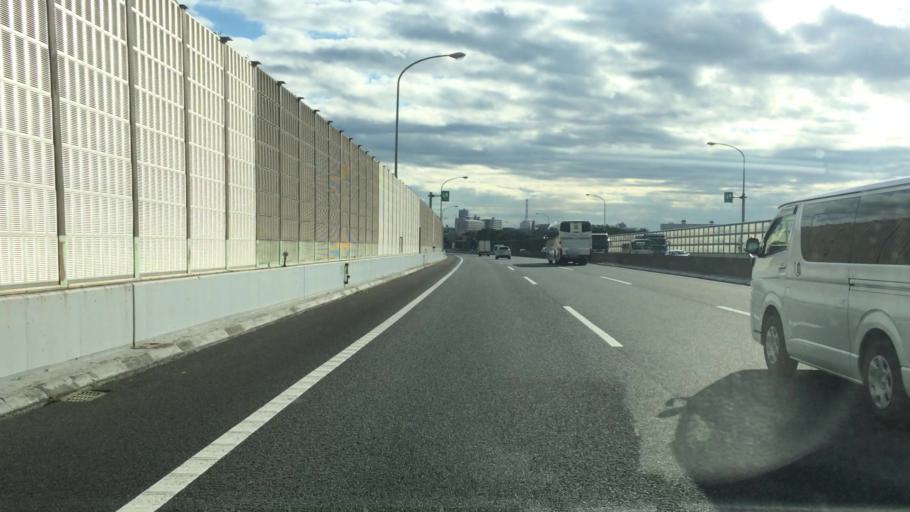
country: JP
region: Chiba
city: Funabashi
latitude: 35.6518
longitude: 140.0488
